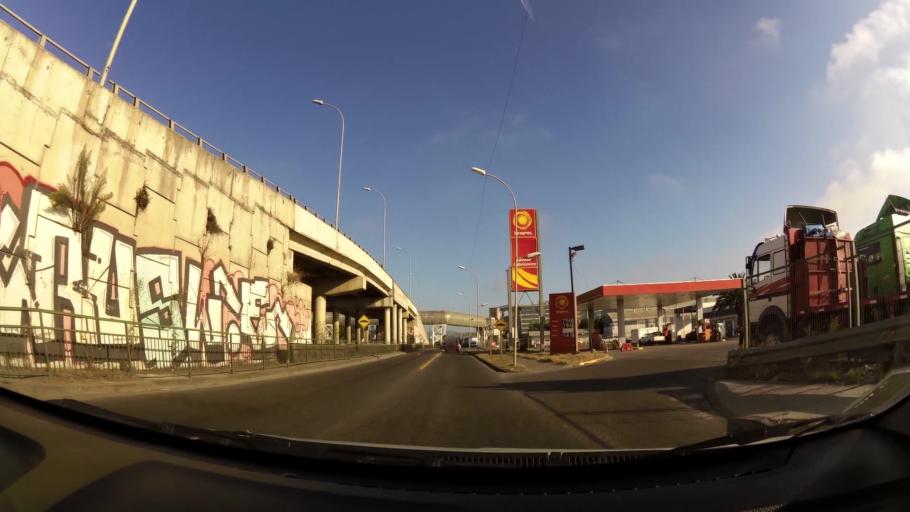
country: CL
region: Biobio
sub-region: Provincia de Concepcion
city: Concepcion
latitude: -36.7905
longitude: -73.0714
